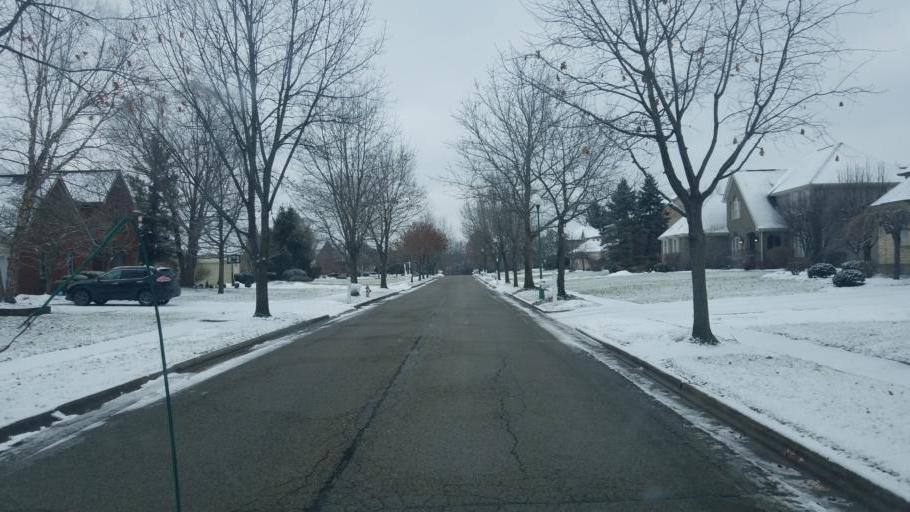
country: US
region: Ohio
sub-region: Franklin County
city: New Albany
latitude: 40.0487
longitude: -82.8295
